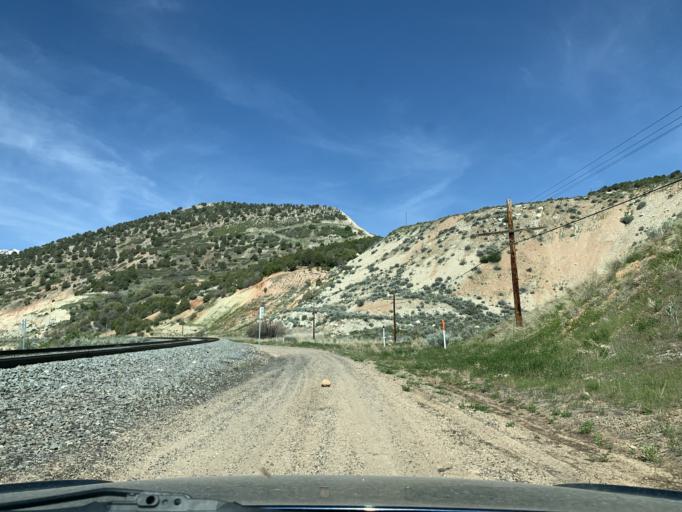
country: US
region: Utah
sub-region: Utah County
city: Mapleton
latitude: 39.9987
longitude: -111.4828
